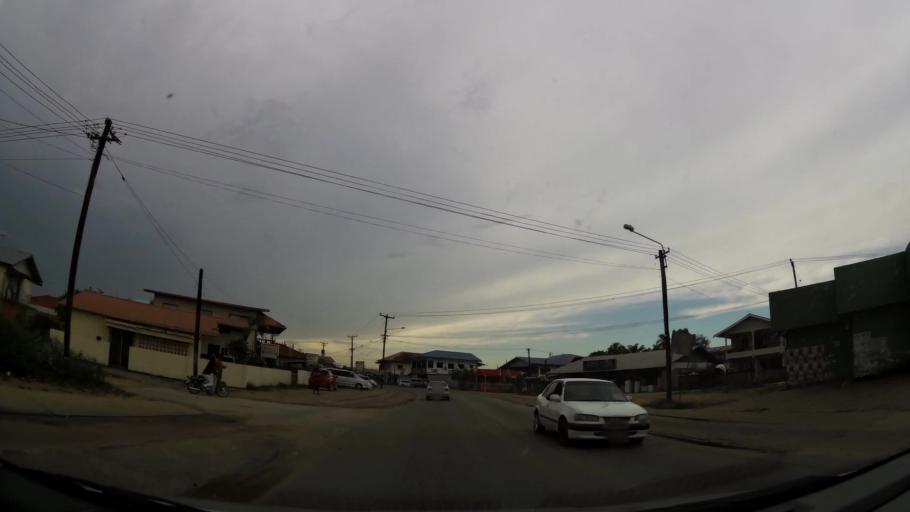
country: SR
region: Paramaribo
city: Paramaribo
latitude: 5.7924
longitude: -55.1898
